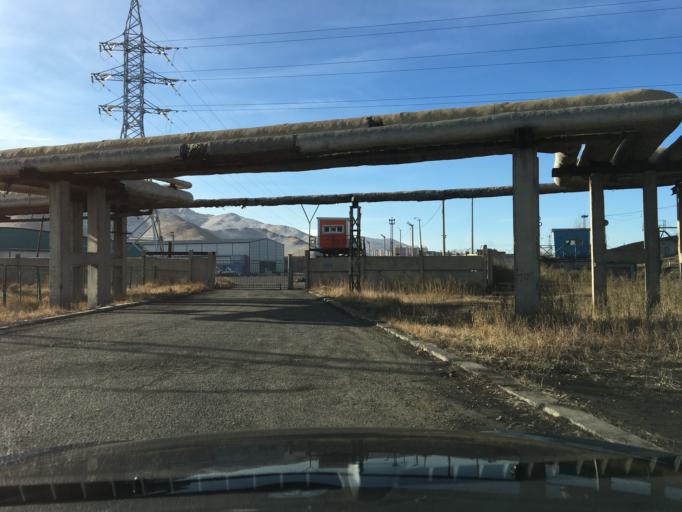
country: MN
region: Ulaanbaatar
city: Ulaanbaatar
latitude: 47.8963
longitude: 106.8719
